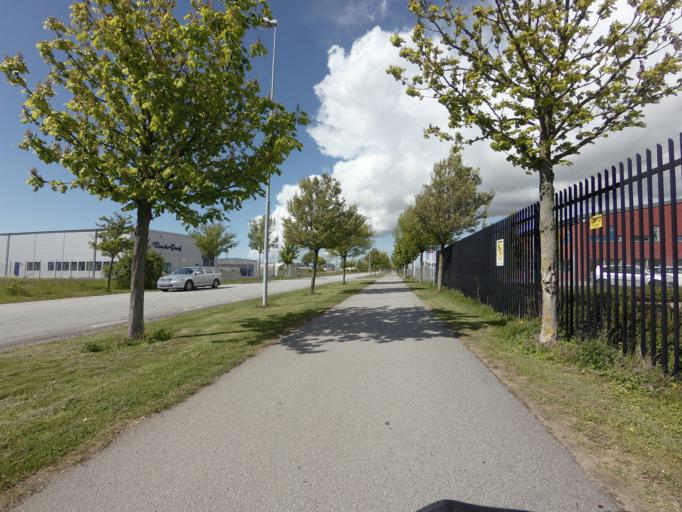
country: SE
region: Skane
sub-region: Landskrona
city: Landskrona
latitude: 55.8829
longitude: 12.8543
